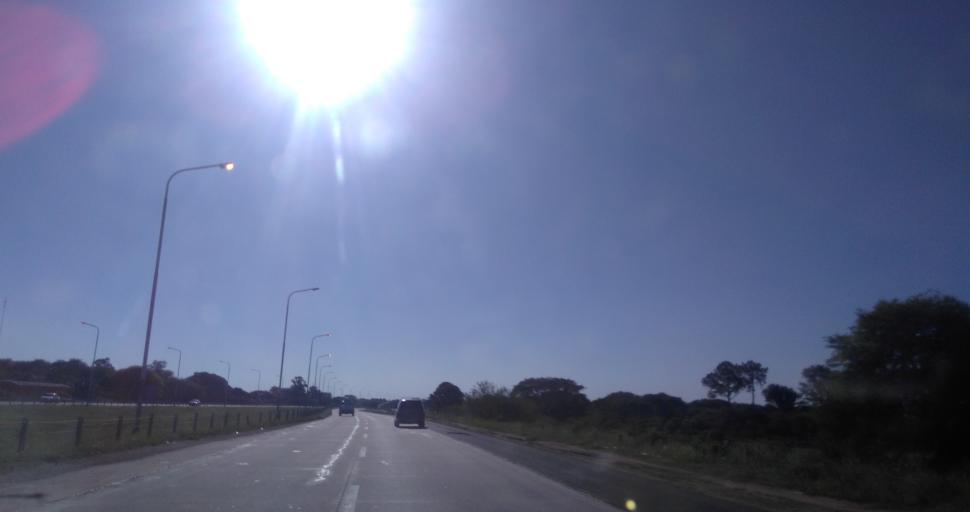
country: AR
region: Chaco
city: Barranqueras
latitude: -27.4365
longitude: -58.9103
